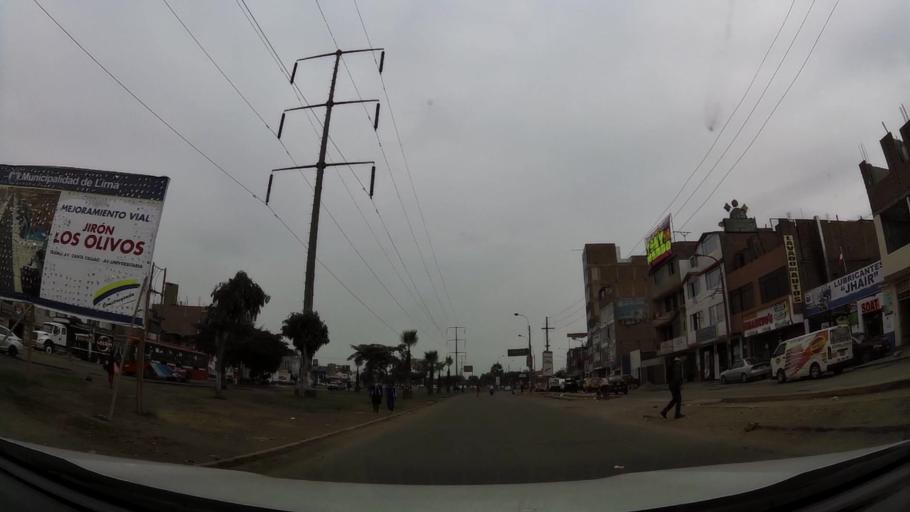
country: PE
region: Lima
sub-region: Lima
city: Independencia
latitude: -11.9888
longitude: -77.0812
